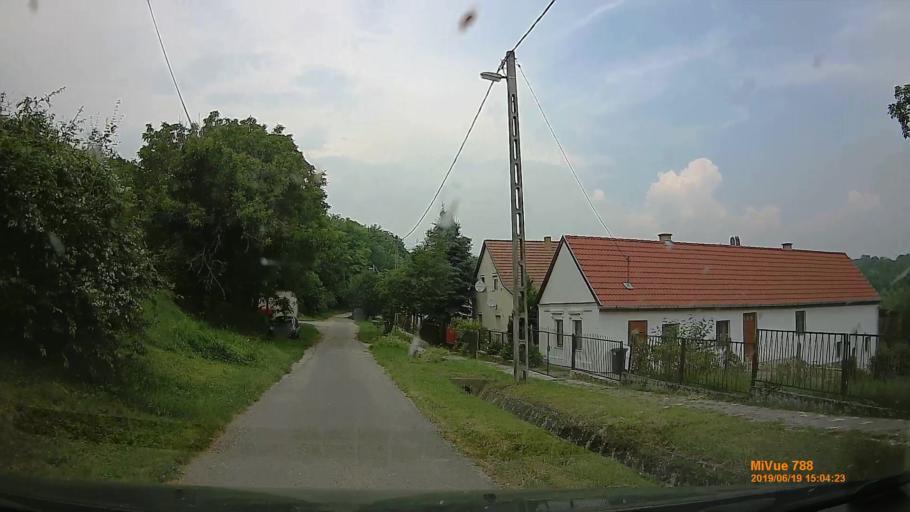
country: HU
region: Baranya
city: Szigetvar
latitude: 46.0992
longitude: 17.8067
